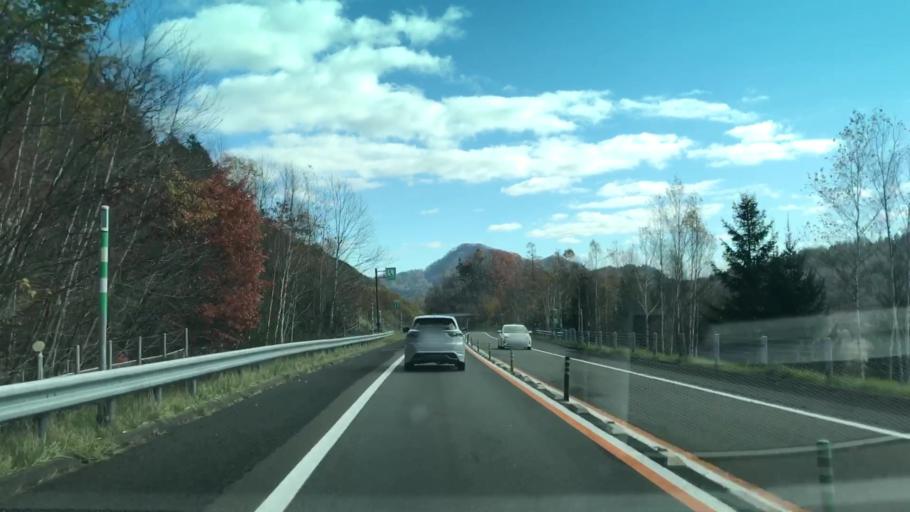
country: JP
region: Hokkaido
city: Chitose
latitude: 42.9115
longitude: 141.9784
